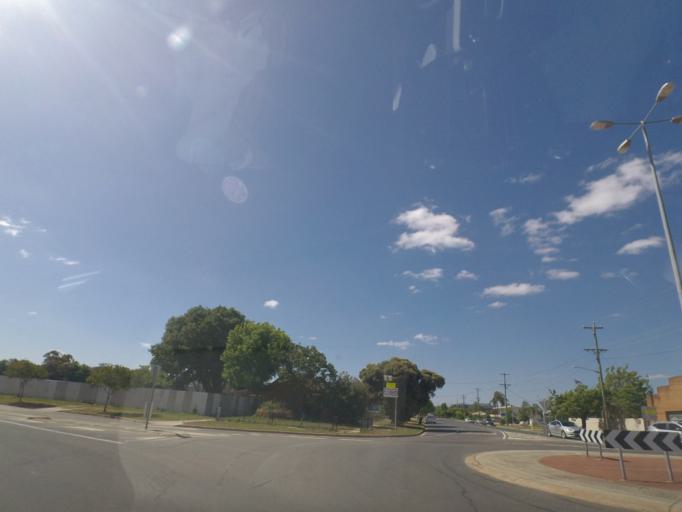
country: AU
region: New South Wales
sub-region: Albury Municipality
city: South Albury
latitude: -36.0911
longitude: 146.9136
